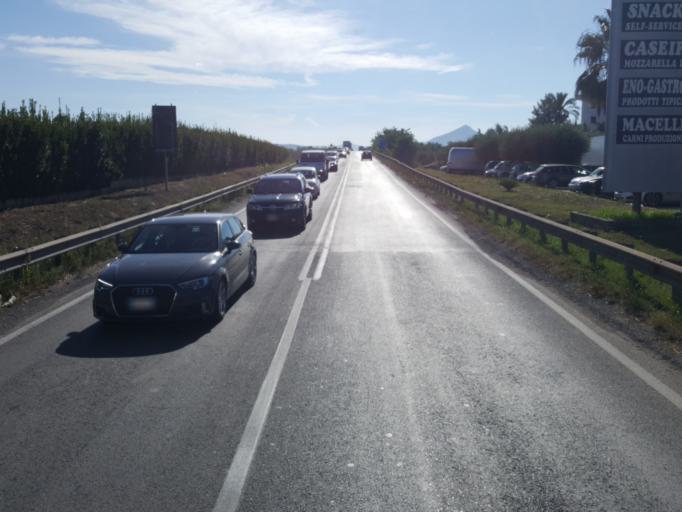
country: IT
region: Campania
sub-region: Provincia di Caserta
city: Pignataro Maggiore
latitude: 41.1642
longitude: 14.1652
